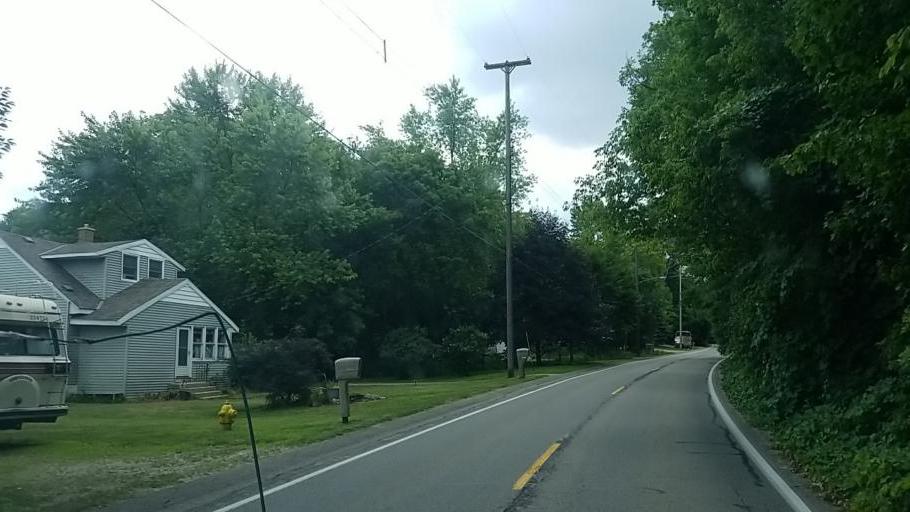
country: US
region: Michigan
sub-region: Kent County
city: Grand Rapids
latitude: 42.9911
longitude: -85.7131
